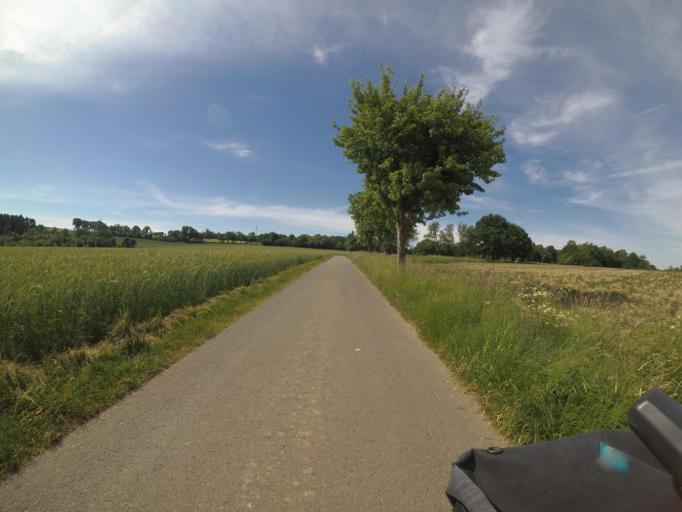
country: DE
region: Rheinland-Pfalz
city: Morbach
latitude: 49.8143
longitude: 7.0887
